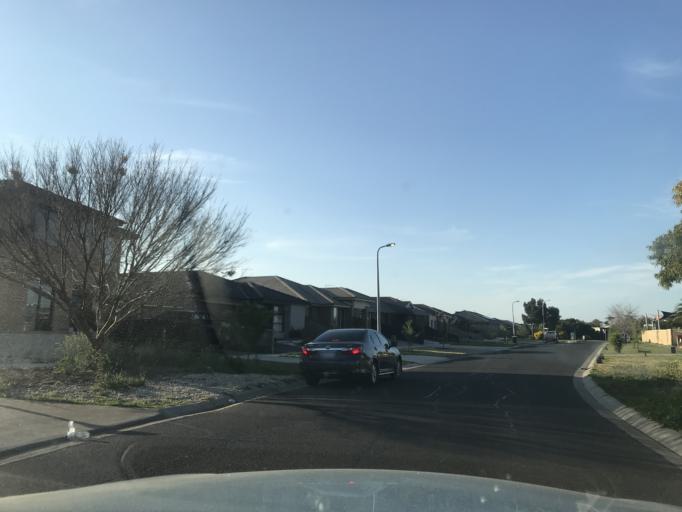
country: AU
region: Victoria
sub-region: Wyndham
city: Williams Landing
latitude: -37.8598
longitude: 144.7274
